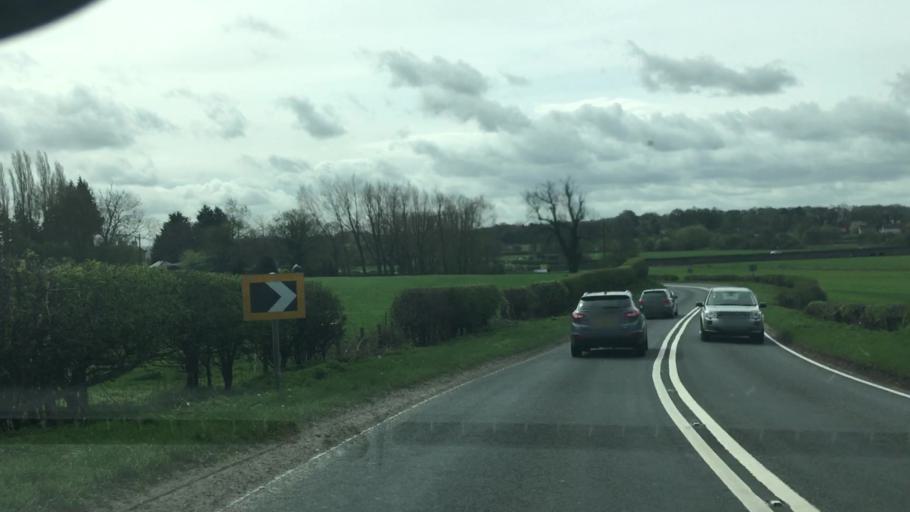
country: GB
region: England
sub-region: City and Borough of Leeds
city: Collingham
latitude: 53.9585
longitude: -1.4417
